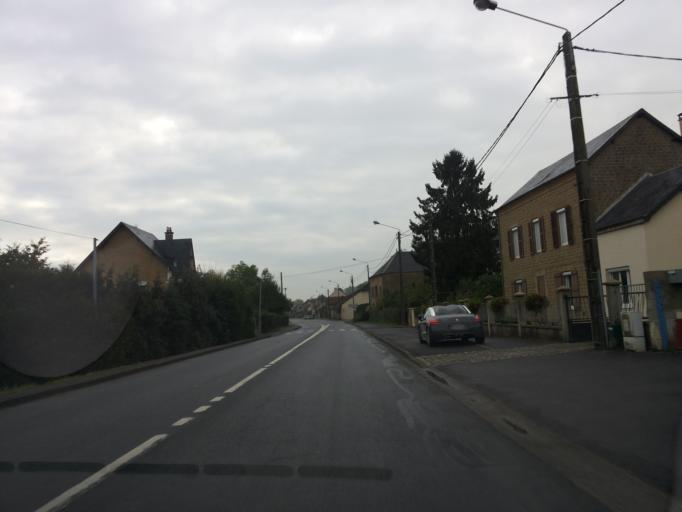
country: FR
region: Champagne-Ardenne
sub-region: Departement des Ardennes
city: Donchery
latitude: 49.6921
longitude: 4.8709
